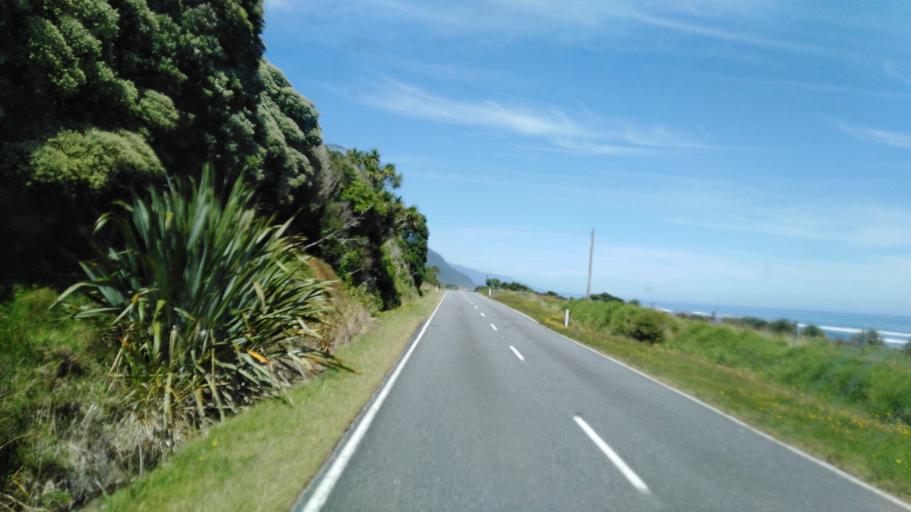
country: NZ
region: West Coast
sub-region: Buller District
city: Westport
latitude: -41.5805
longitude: 171.8985
